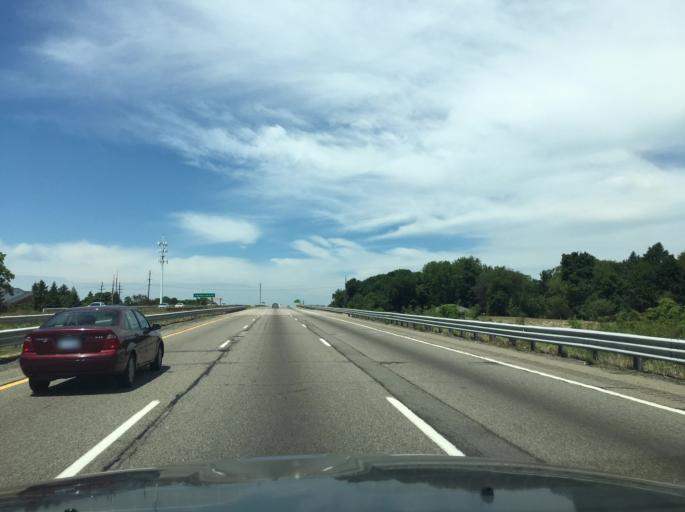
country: US
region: Michigan
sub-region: Oakland County
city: Bloomfield Hills
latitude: 42.6058
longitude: -83.2042
